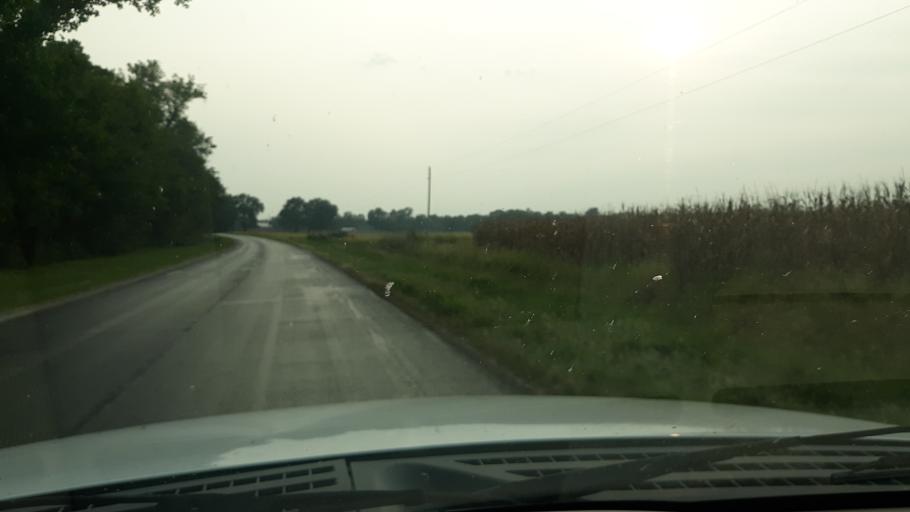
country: US
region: Illinois
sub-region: Edwards County
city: Grayville
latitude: 38.2921
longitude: -87.9725
